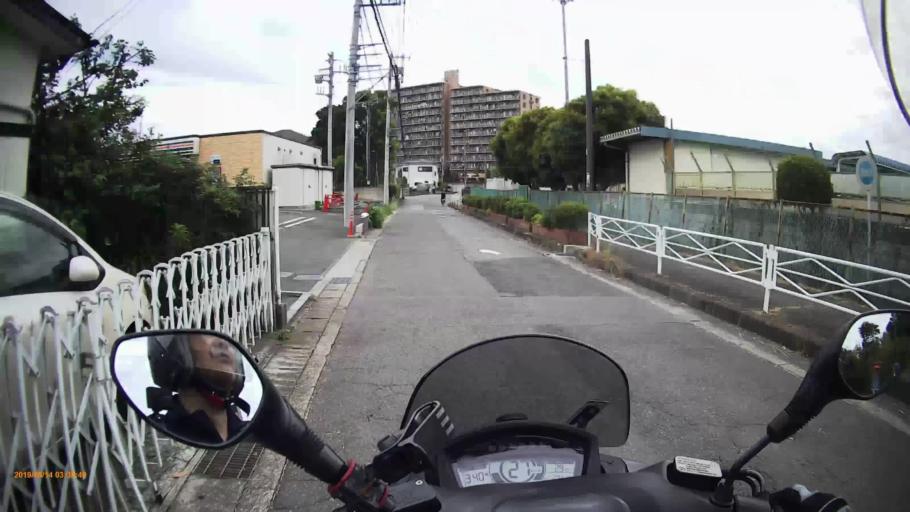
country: JP
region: Kanagawa
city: Minami-rinkan
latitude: 35.4176
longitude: 139.4478
